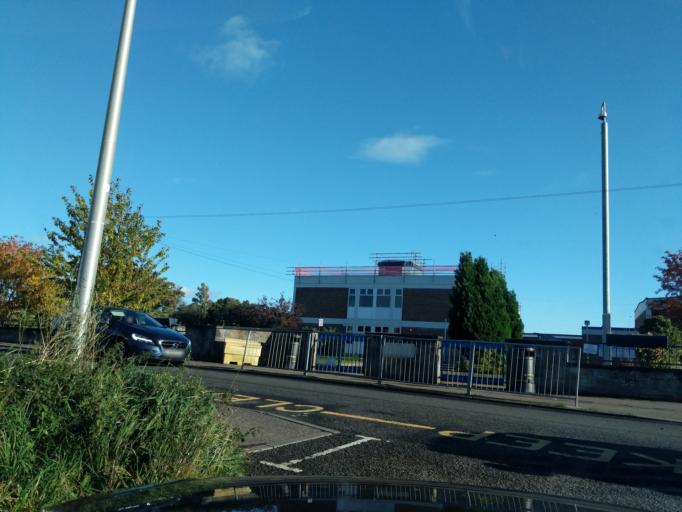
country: GB
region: Scotland
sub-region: Fife
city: Leuchars
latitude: 56.3832
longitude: -2.8819
